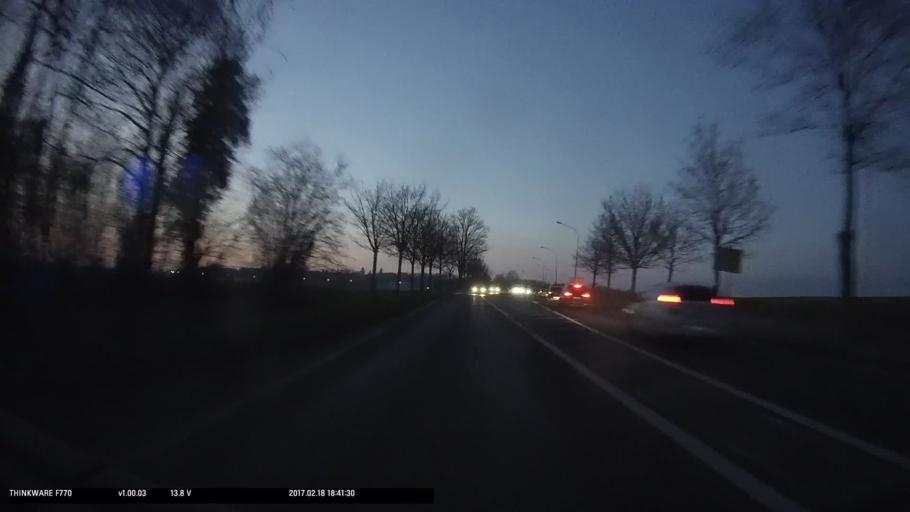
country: FR
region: Ile-de-France
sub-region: Departement du Val-d'Oise
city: Ableiges
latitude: 49.1076
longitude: 2.0336
